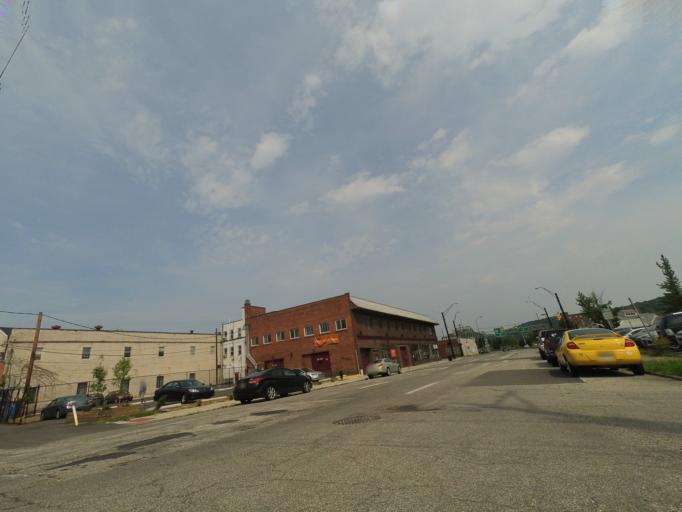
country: US
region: West Virginia
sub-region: Cabell County
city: Huntington
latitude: 38.4192
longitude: -82.4487
